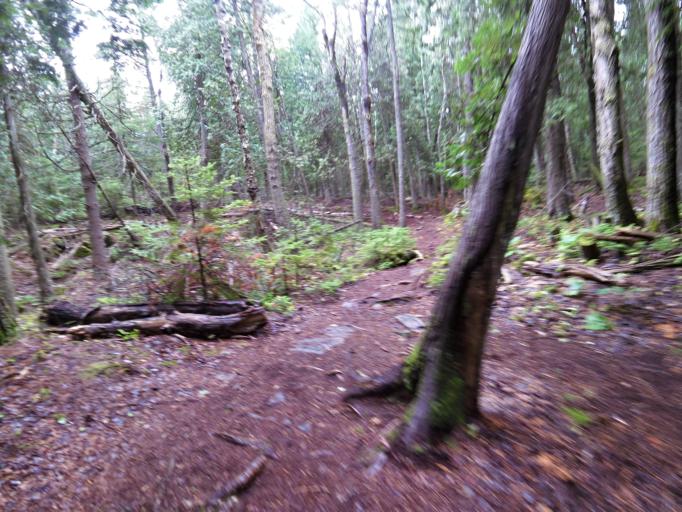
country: CA
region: Ontario
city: Tobermory
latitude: 45.2592
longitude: -81.6481
